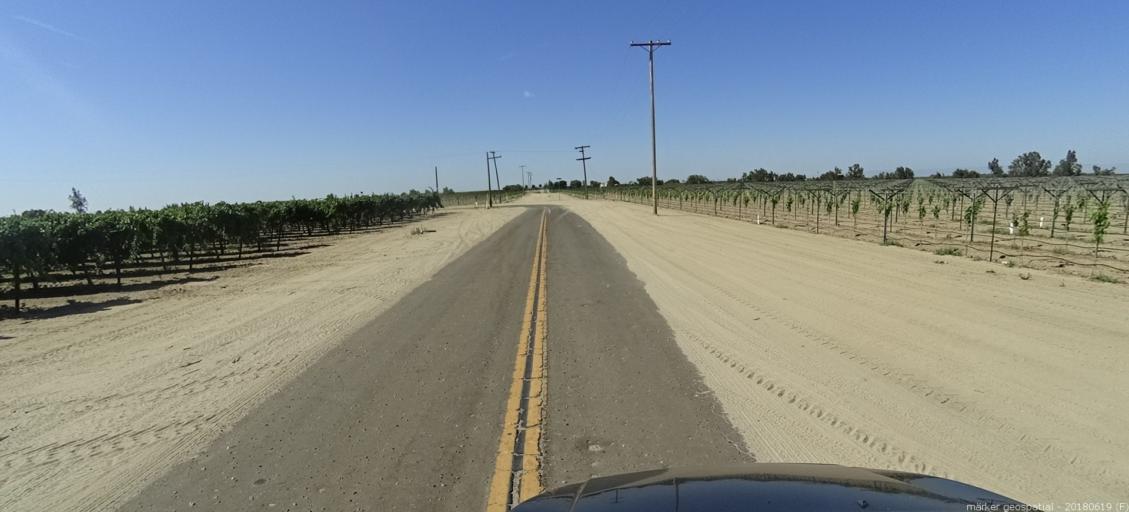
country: US
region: California
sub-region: Fresno County
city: Biola
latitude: 36.8230
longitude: -120.0428
